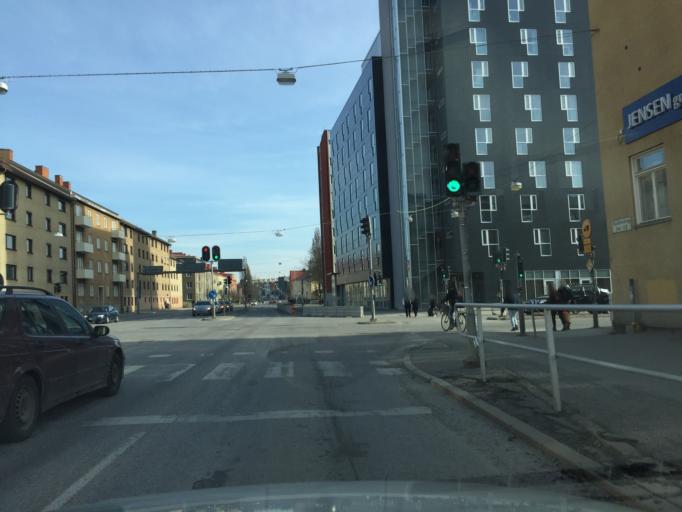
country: SE
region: OErebro
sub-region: Orebro Kommun
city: Orebro
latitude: 59.2684
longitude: 15.2150
